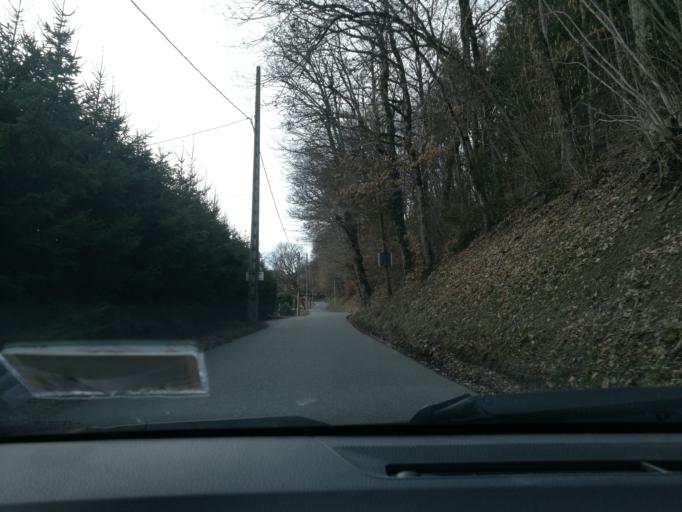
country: FR
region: Rhone-Alpes
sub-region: Departement de la Haute-Savoie
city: Cordon
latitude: 45.9263
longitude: 6.6280
